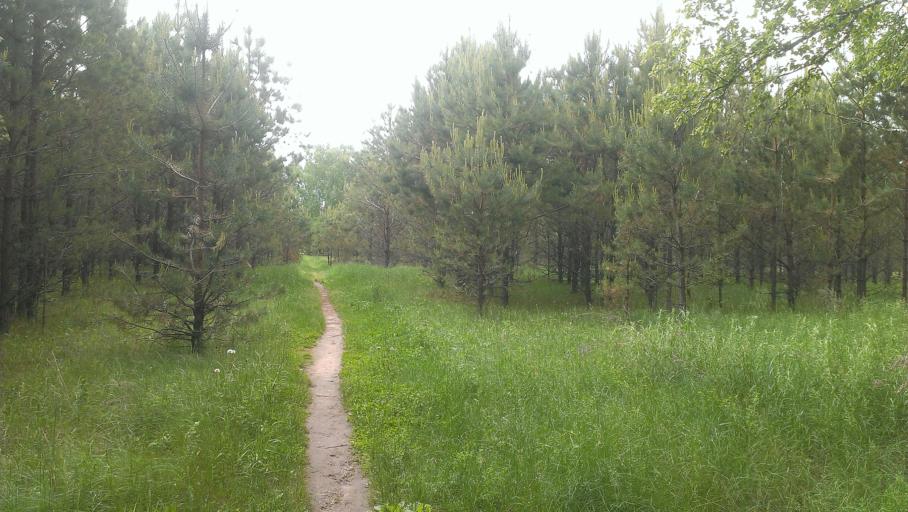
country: RU
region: Altai Krai
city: Bayunovskiye Klyuchi
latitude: 53.3345
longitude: 84.0981
